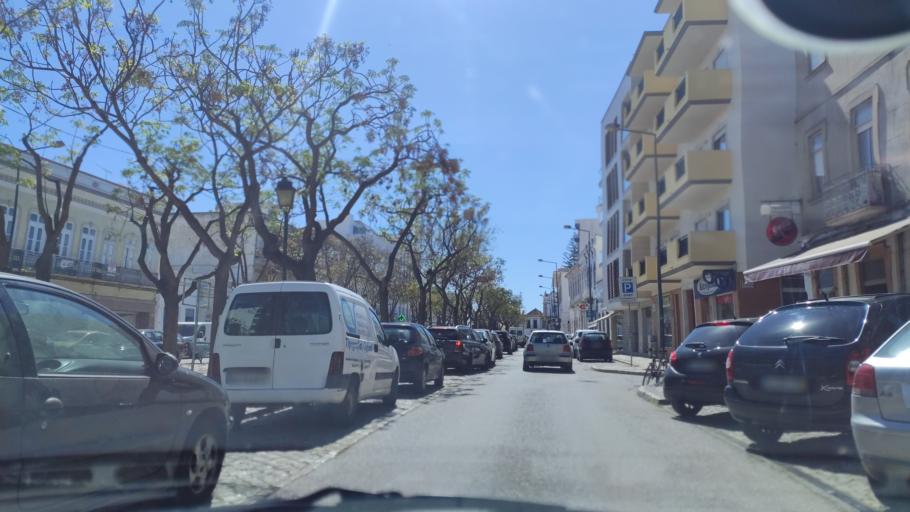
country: PT
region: Faro
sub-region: Olhao
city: Olhao
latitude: 37.0284
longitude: -7.8395
